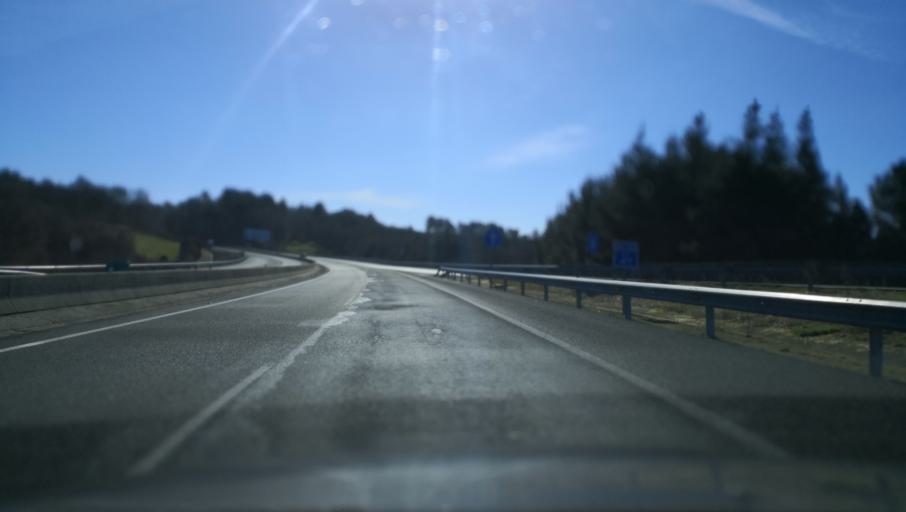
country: ES
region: Galicia
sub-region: Provincia de Pontevedra
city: Lalin
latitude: 42.6362
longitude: -8.1309
